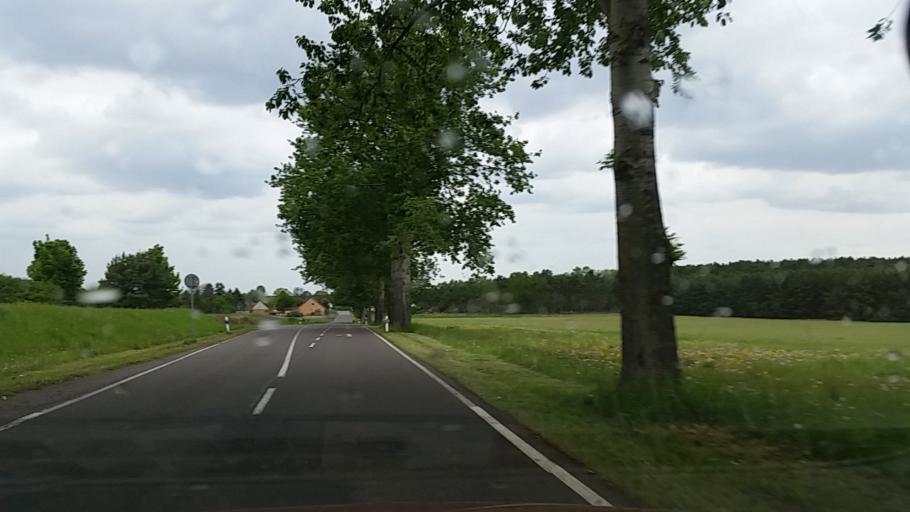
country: DE
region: Brandenburg
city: Rauen
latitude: 52.3200
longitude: 13.9609
